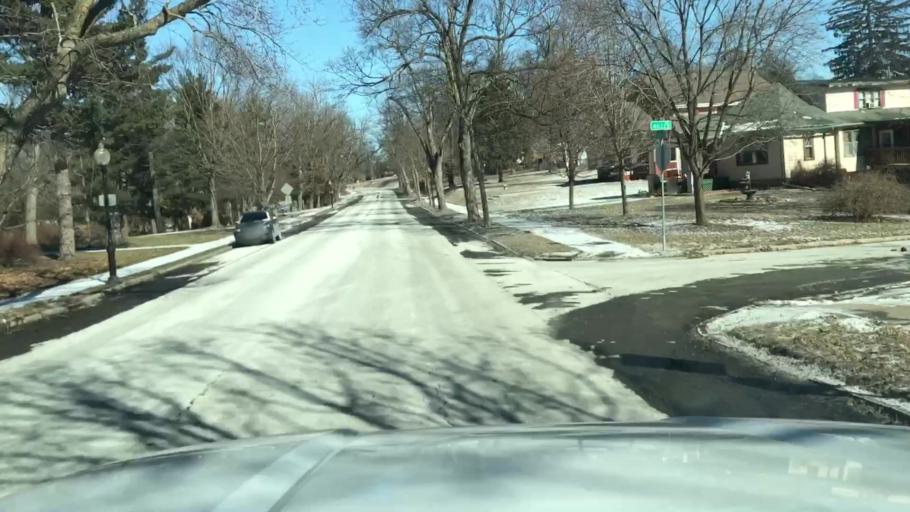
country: US
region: Missouri
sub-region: Buchanan County
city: Saint Joseph
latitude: 39.7932
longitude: -94.8204
